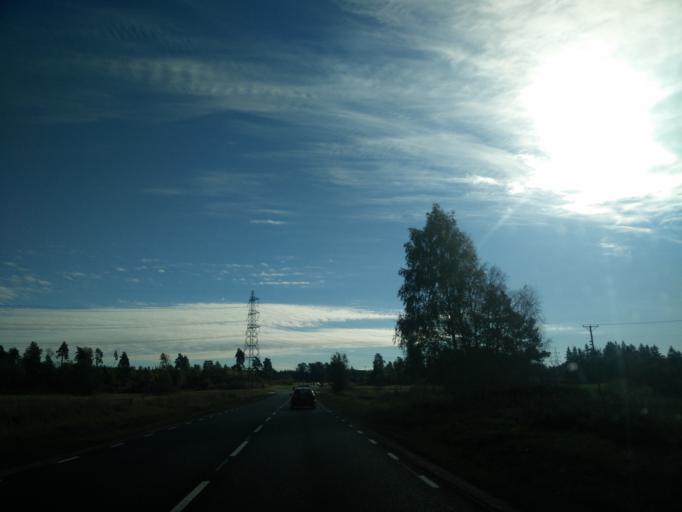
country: SE
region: Stockholm
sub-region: Upplands Vasby Kommun
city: Upplands Vaesby
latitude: 59.5074
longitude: 17.9687
